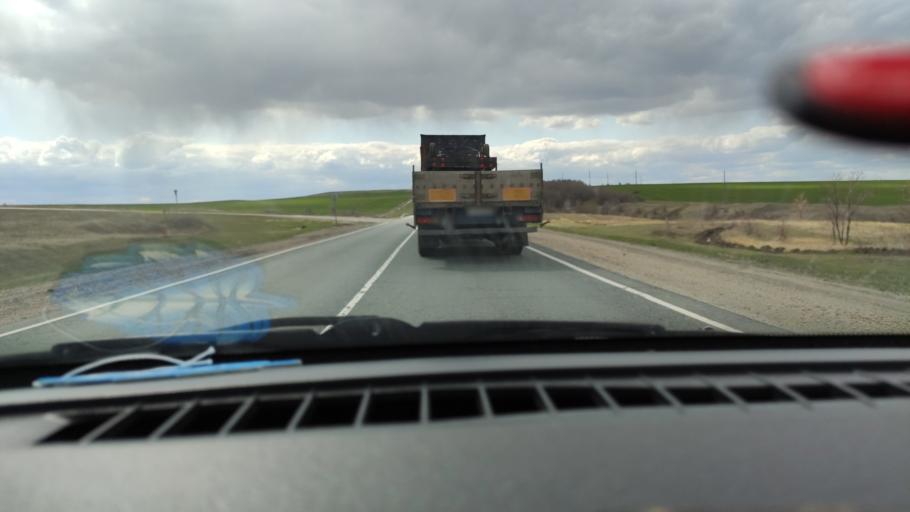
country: RU
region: Saratov
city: Alekseyevka
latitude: 52.2260
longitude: 47.9016
